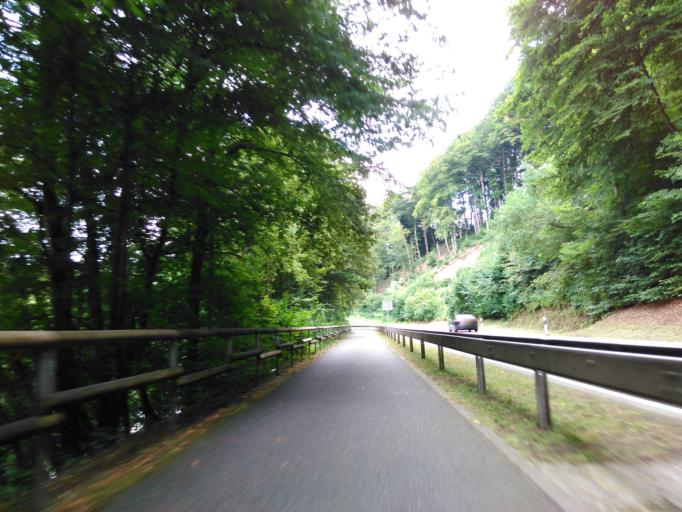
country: DE
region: Rheinland-Pfalz
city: Ralingen
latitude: 49.8111
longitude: 6.4905
